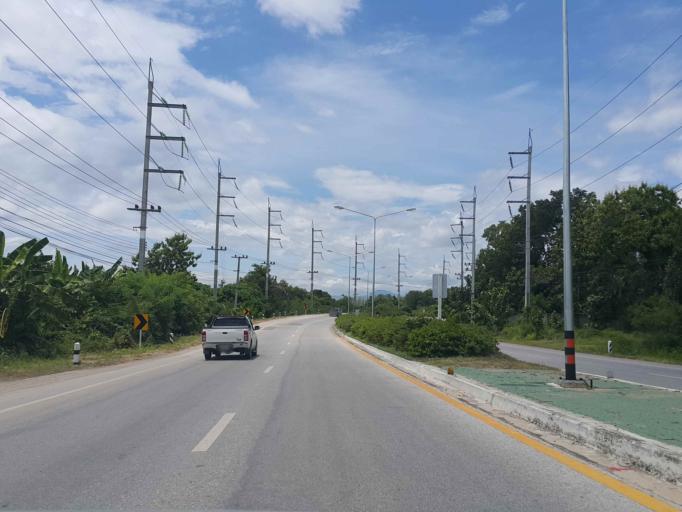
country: TH
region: Lamphun
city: Ban Hong
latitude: 18.3438
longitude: 98.8112
